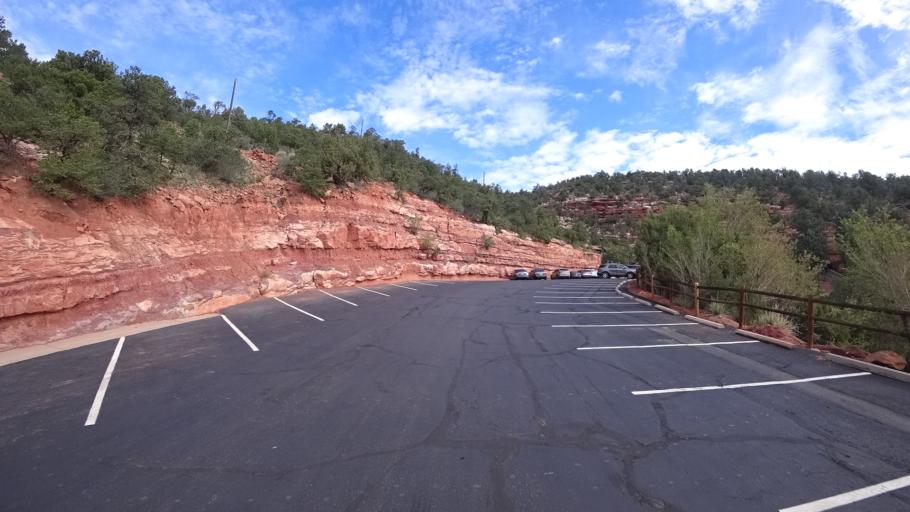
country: US
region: Colorado
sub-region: El Paso County
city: Manitou Springs
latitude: 38.8625
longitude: -104.9129
